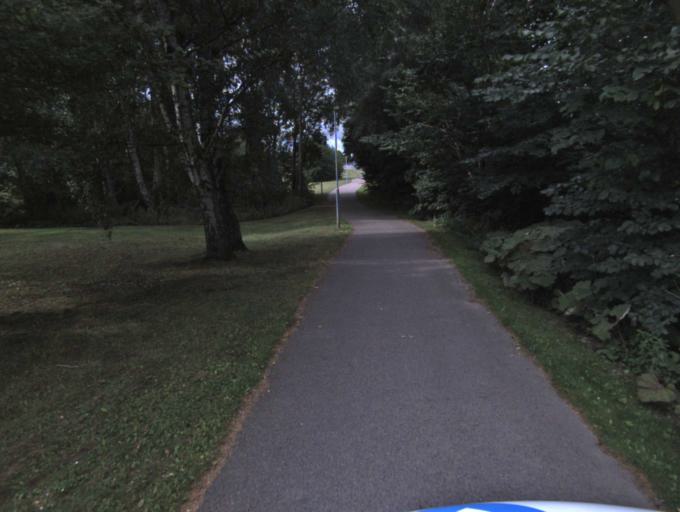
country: SE
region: Skane
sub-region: Kavlinge Kommun
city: Kaevlinge
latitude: 55.7810
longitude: 13.1043
